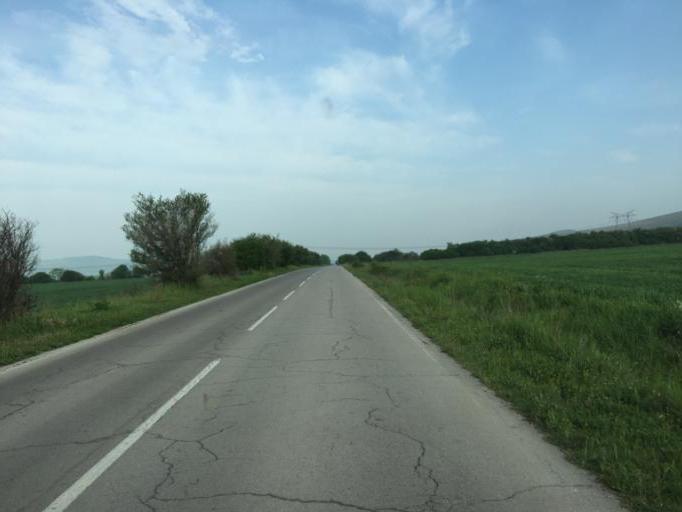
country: BG
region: Kyustendil
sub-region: Obshtina Bobovdol
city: Bobovdol
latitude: 42.4544
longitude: 23.1067
